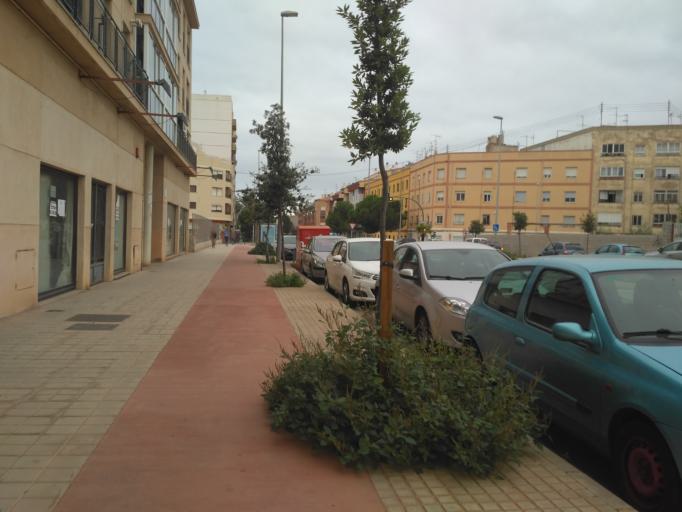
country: ES
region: Valencia
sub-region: Provincia de Castello
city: Castello de la Plana
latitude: 39.9879
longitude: -0.0639
